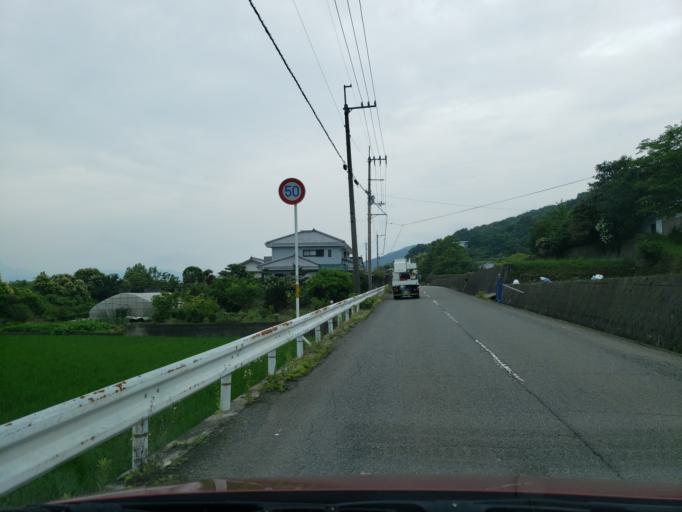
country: JP
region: Tokushima
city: Wakimachi
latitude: 34.1036
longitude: 134.2356
